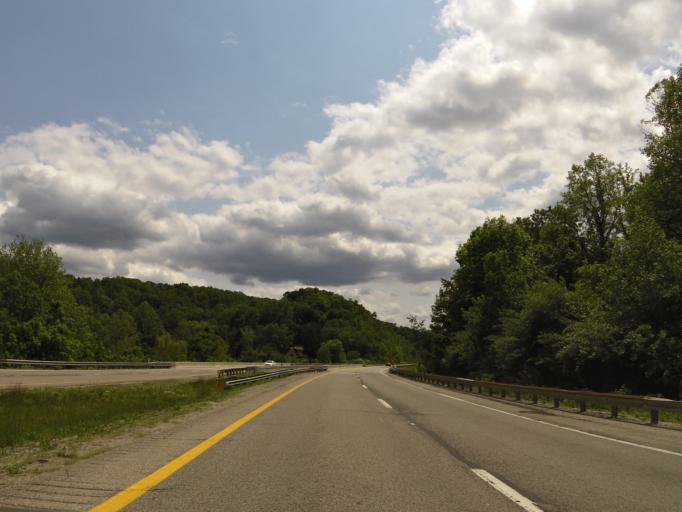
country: US
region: West Virginia
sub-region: Kanawha County
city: Sissonville
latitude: 38.4785
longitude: -81.6433
